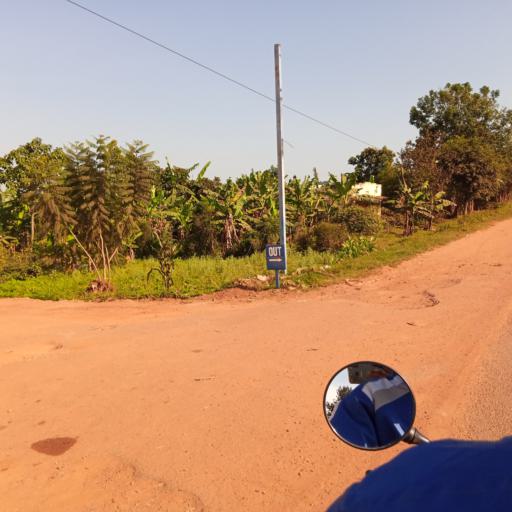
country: UG
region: Central Region
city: Masaka
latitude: -0.4459
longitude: 31.6673
